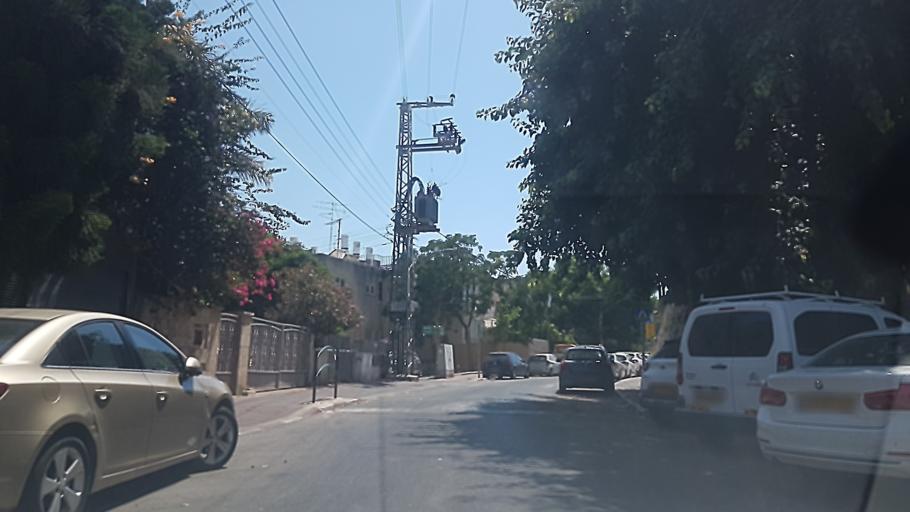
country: IL
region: Tel Aviv
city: Bene Beraq
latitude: 32.0805
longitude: 34.8245
